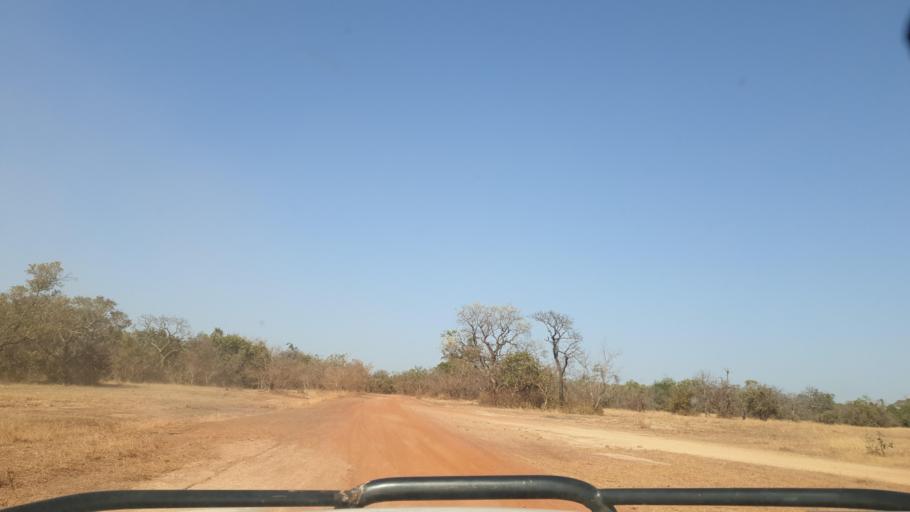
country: ML
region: Sikasso
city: Bougouni
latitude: 11.8202
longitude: -6.9501
